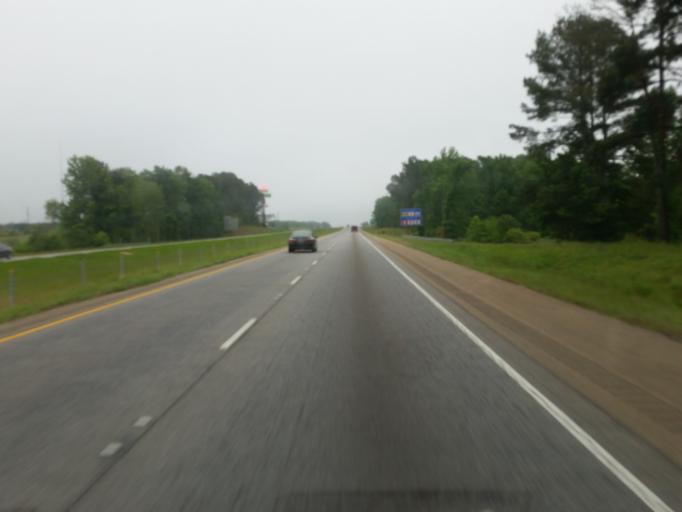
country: US
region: Louisiana
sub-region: Webster Parish
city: Minden
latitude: 32.5824
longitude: -93.2576
